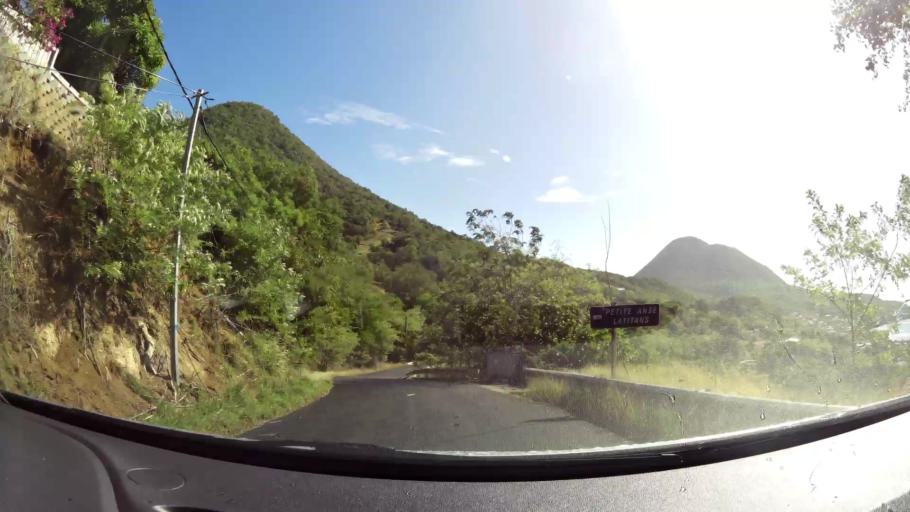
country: MQ
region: Martinique
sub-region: Martinique
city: Les Trois-Ilets
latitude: 14.4759
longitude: -61.0744
